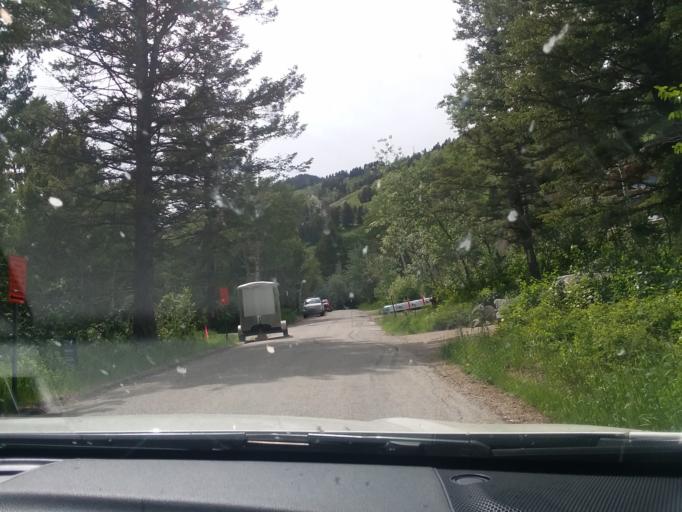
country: US
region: Wyoming
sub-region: Teton County
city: Moose Wilson Road
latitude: 43.5884
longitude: -110.8375
